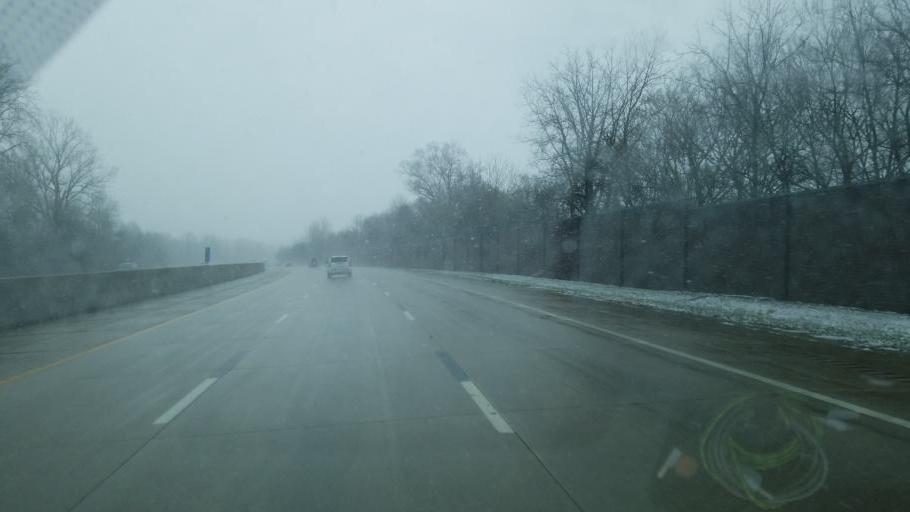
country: US
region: Ohio
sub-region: Montgomery County
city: Huber Heights
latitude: 39.8672
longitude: -84.1582
